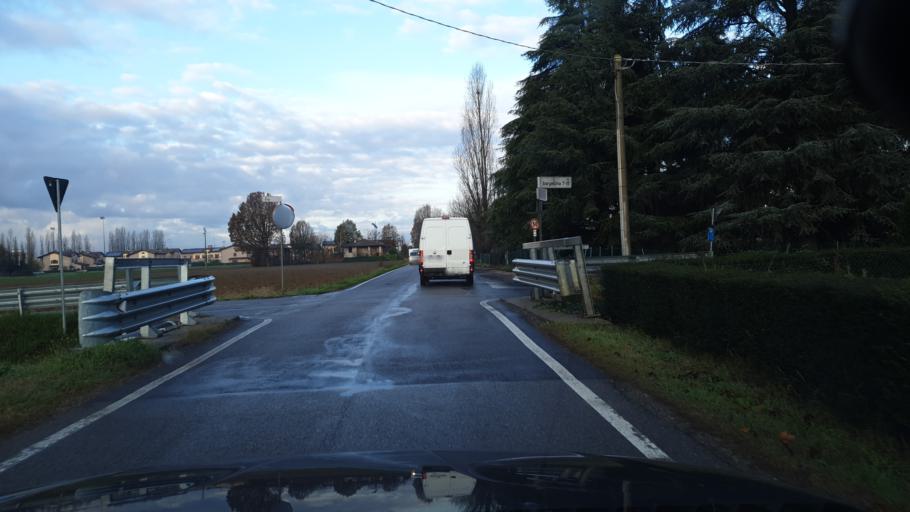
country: IT
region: Emilia-Romagna
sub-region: Provincia di Bologna
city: Crespellano
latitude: 44.5178
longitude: 11.1344
